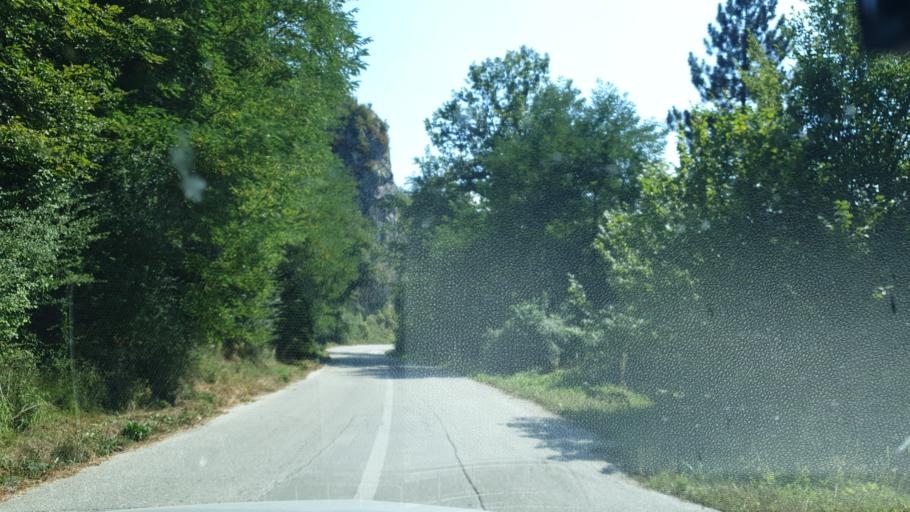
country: RS
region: Central Serbia
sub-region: Zlatiborski Okrug
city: Cajetina
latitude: 43.6710
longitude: 19.8288
